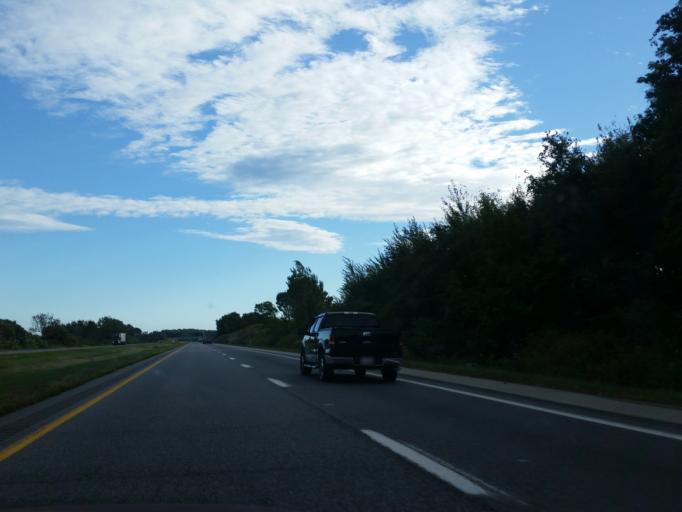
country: US
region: Pennsylvania
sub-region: Erie County
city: North East
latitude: 42.2159
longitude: -79.7953
